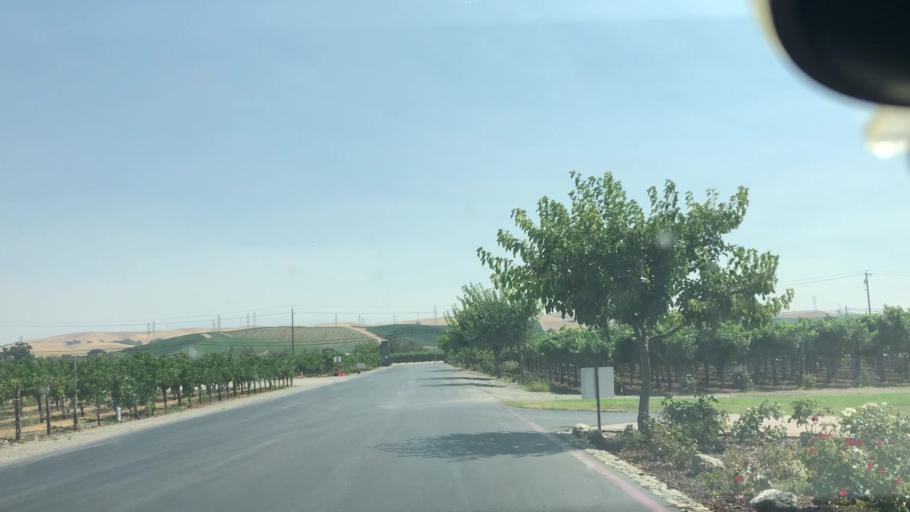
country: US
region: California
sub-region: Alameda County
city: Livermore
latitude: 37.6667
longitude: -121.7389
